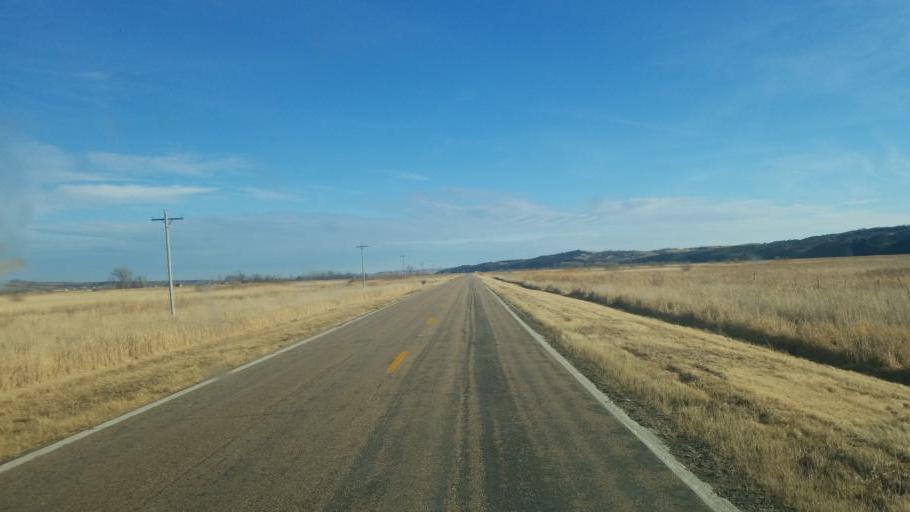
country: US
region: South Dakota
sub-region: Bon Homme County
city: Springfield
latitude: 42.7925
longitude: -98.1130
